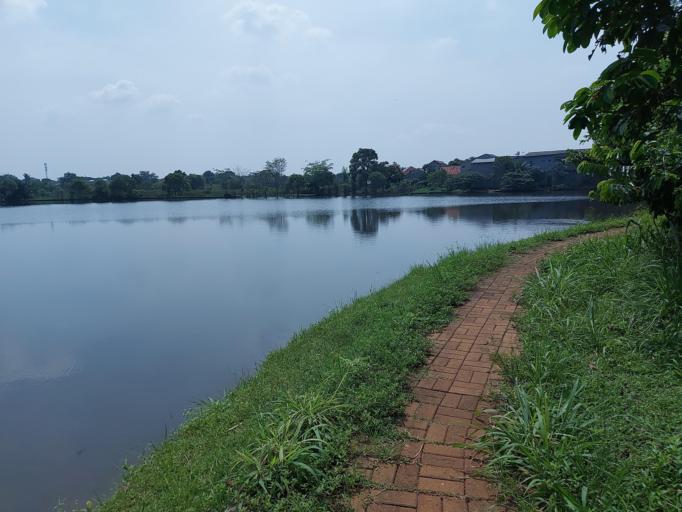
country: ID
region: West Java
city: Cibinong
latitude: -6.4800
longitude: 106.8326
